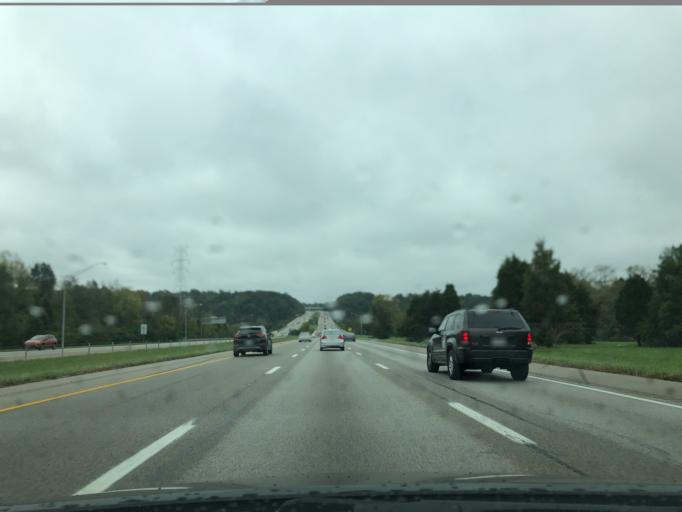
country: US
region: Ohio
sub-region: Hamilton County
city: The Village of Indian Hill
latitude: 39.2436
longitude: -84.3020
